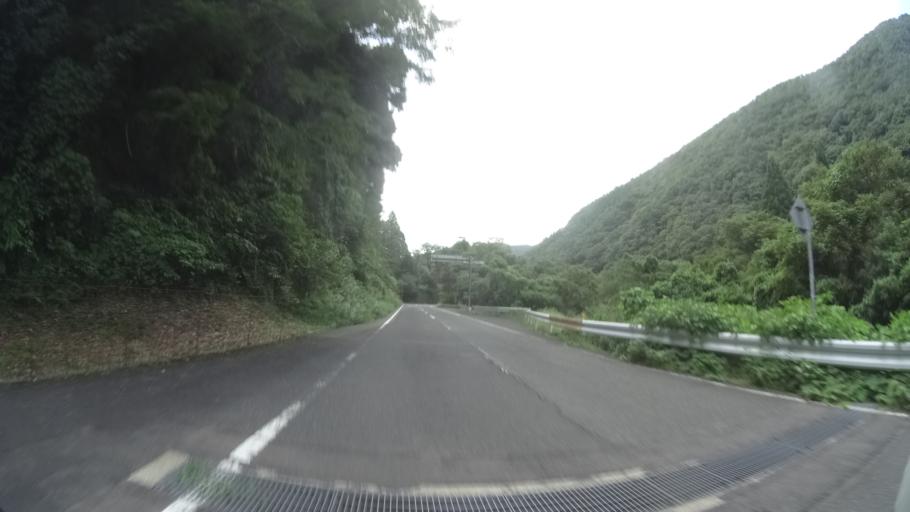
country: JP
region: Tottori
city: Kurayoshi
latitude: 35.4012
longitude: 133.9390
